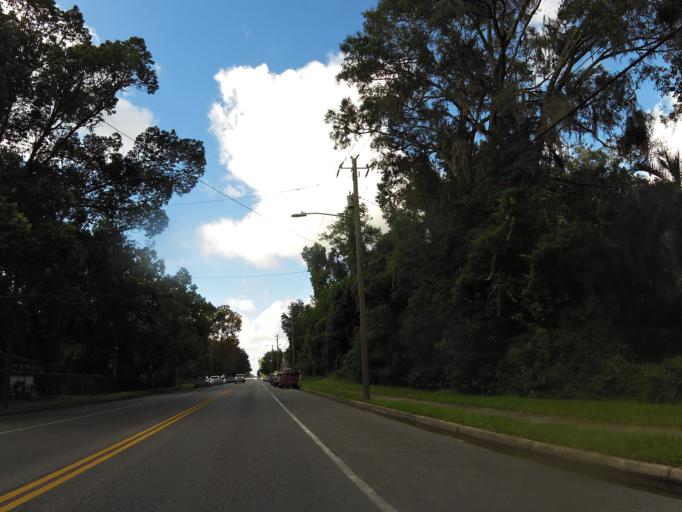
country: US
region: Georgia
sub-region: Camden County
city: Kingsland
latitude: 30.8037
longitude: -81.6909
